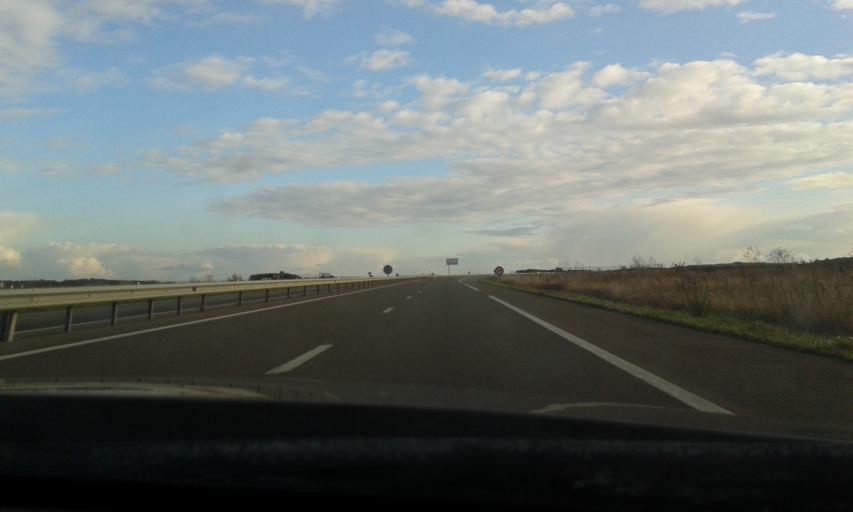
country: FR
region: Centre
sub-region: Departement d'Eure-et-Loir
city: Villemeux-sur-Eure
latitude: 48.6430
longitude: 1.4037
